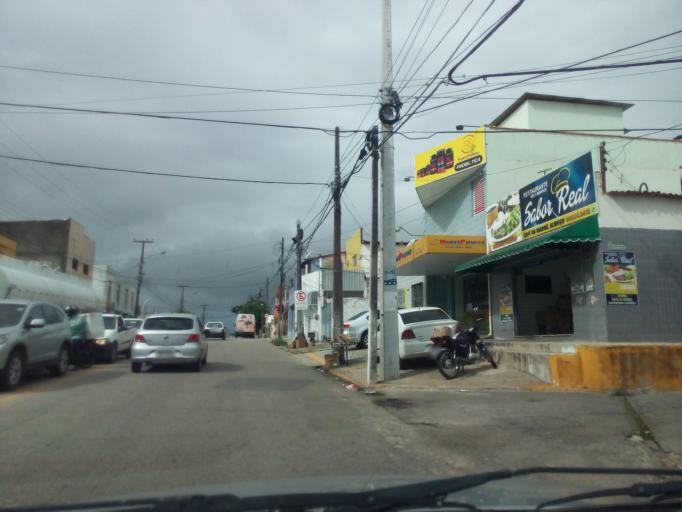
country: BR
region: Rio Grande do Norte
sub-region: Natal
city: Natal
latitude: -5.8094
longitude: -35.2115
